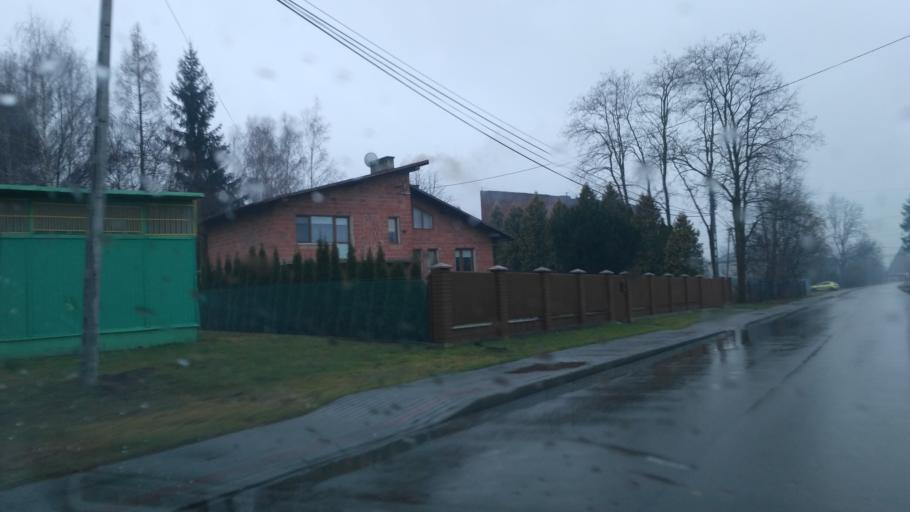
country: PL
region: Subcarpathian Voivodeship
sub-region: Powiat lancucki
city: Krzemienica
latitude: 50.0801
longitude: 22.1401
